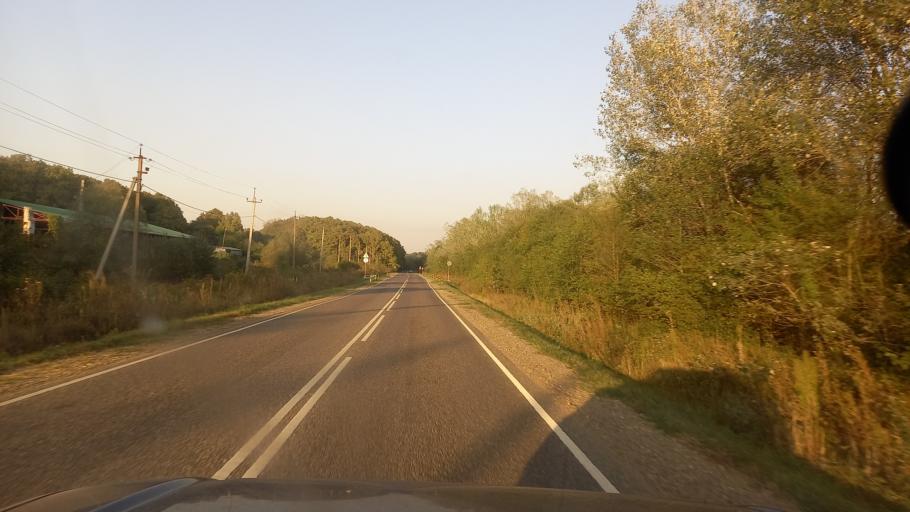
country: RU
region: Krasnodarskiy
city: Smolenskaya
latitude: 44.7475
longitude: 38.7556
